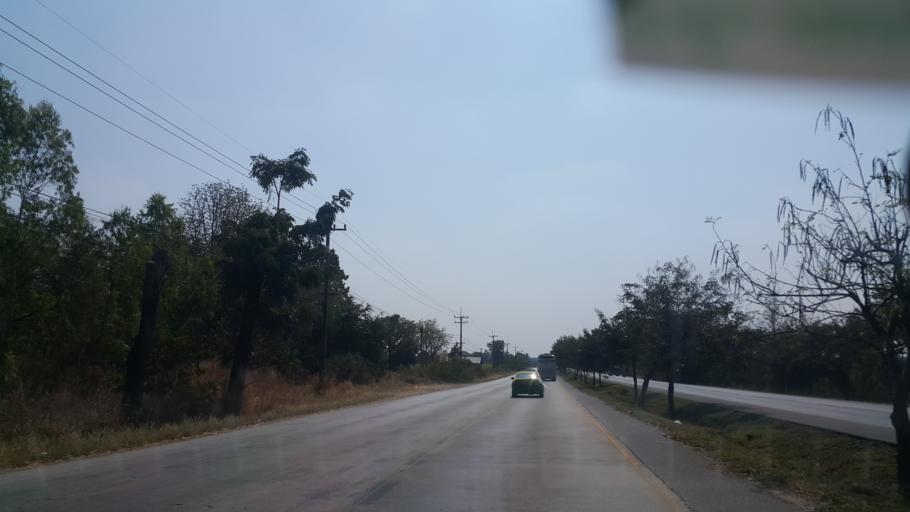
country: TH
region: Nakhon Ratchasima
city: Non Daeng
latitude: 15.3998
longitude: 102.4725
